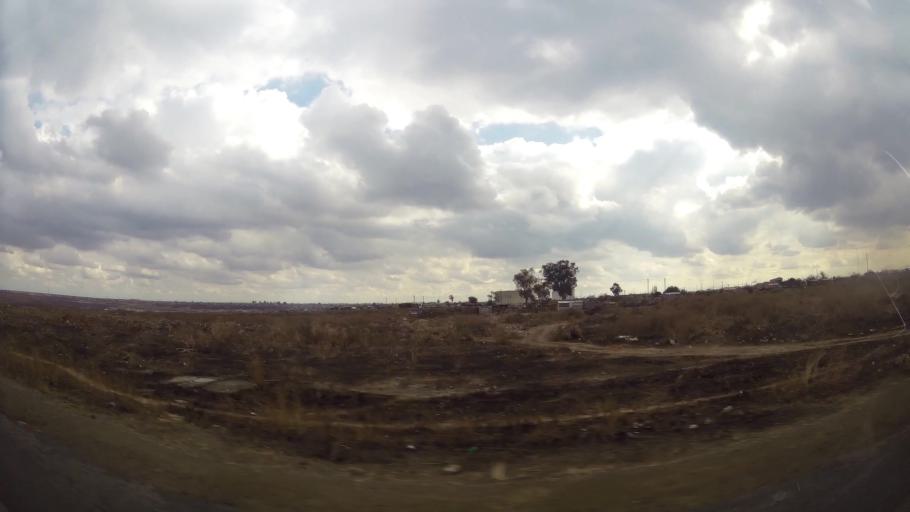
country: ZA
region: Orange Free State
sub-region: Fezile Dabi District Municipality
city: Sasolburg
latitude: -26.8639
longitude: 27.8879
